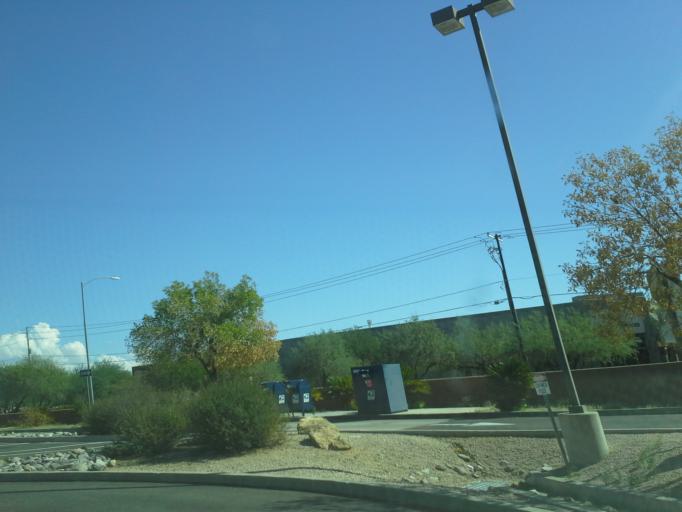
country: US
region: Arizona
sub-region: Maricopa County
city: Paradise Valley
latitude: 33.6772
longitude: -112.0281
